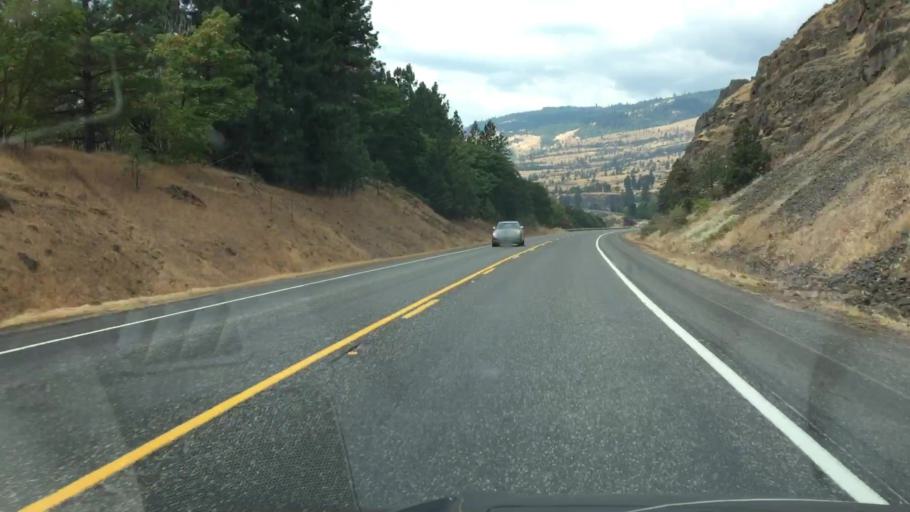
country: US
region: Oregon
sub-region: Wasco County
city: Chenoweth
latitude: 45.7077
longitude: -121.3317
